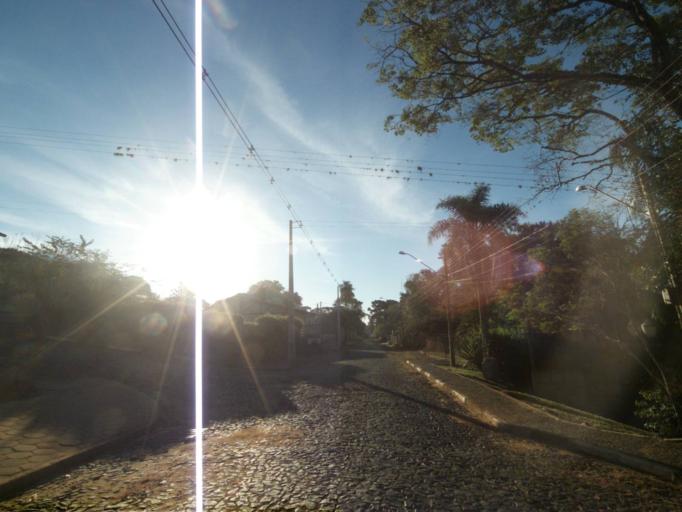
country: BR
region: Parana
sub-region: Tibagi
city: Tibagi
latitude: -24.5145
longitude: -50.4087
